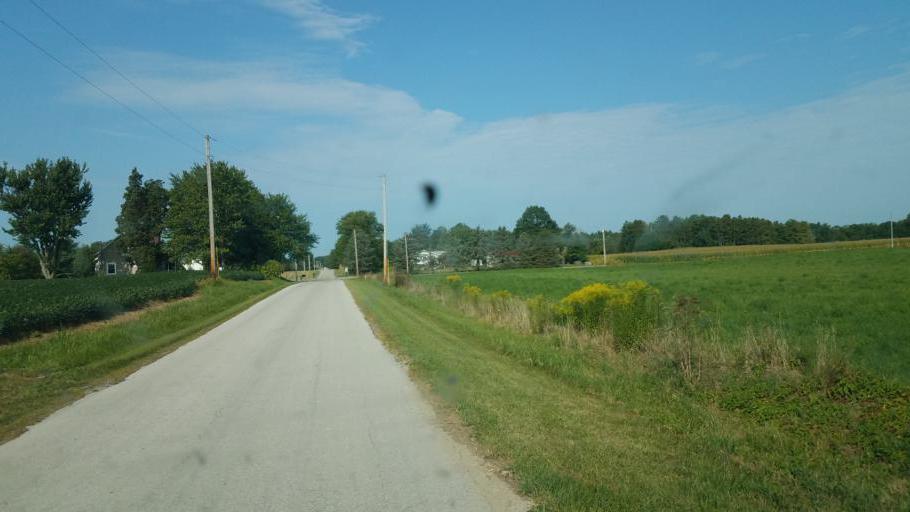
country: US
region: Ohio
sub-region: Morrow County
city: Cardington
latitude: 40.5029
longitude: -82.9372
